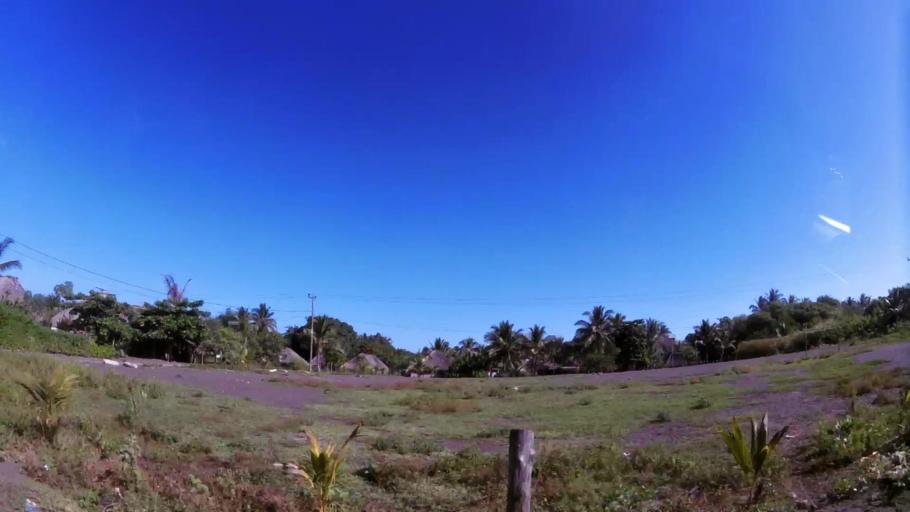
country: GT
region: Santa Rosa
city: Guazacapan
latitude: 13.8611
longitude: -90.4001
